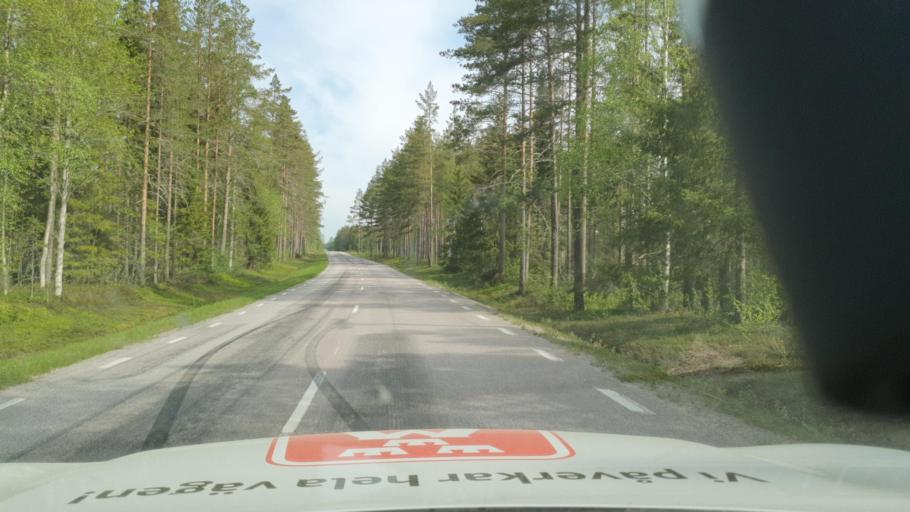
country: SE
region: Vaesterbotten
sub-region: Umea Kommun
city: Hoernefors
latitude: 63.6847
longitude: 19.9190
